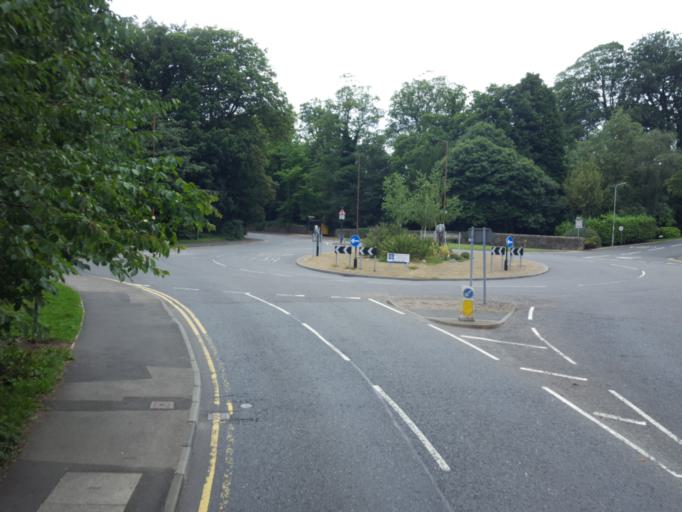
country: GB
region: England
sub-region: County Durham
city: Durham
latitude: 54.7902
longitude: -1.5907
